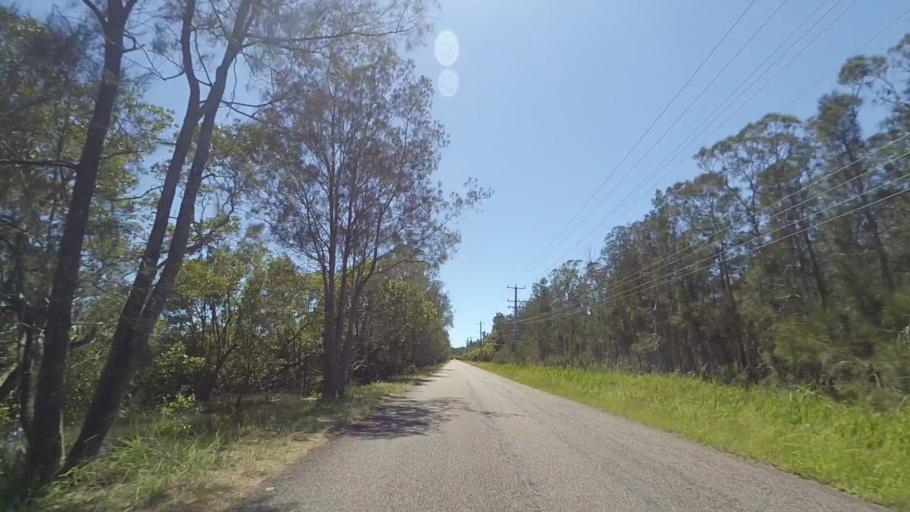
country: AU
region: New South Wales
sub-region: Port Stephens Shire
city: Medowie
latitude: -32.7790
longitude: 151.9621
